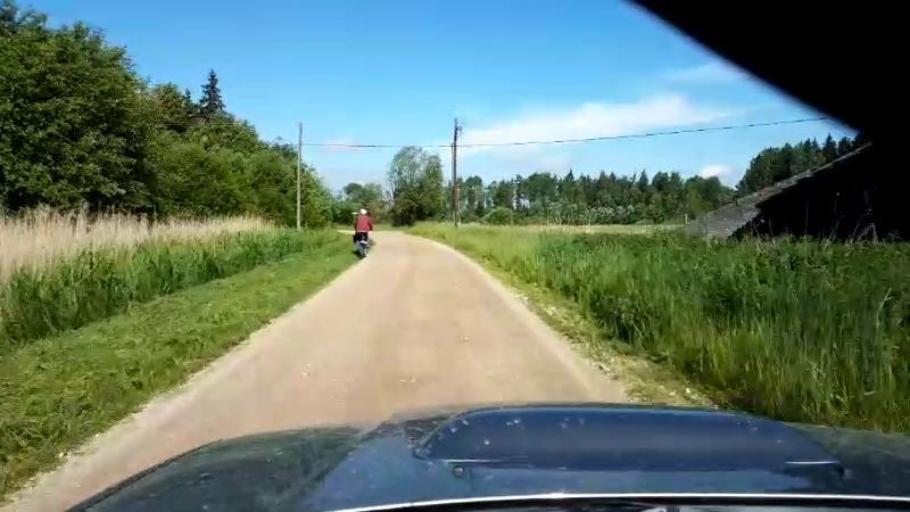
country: EE
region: Paernumaa
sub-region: Sindi linn
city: Sindi
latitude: 58.5173
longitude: 24.6574
